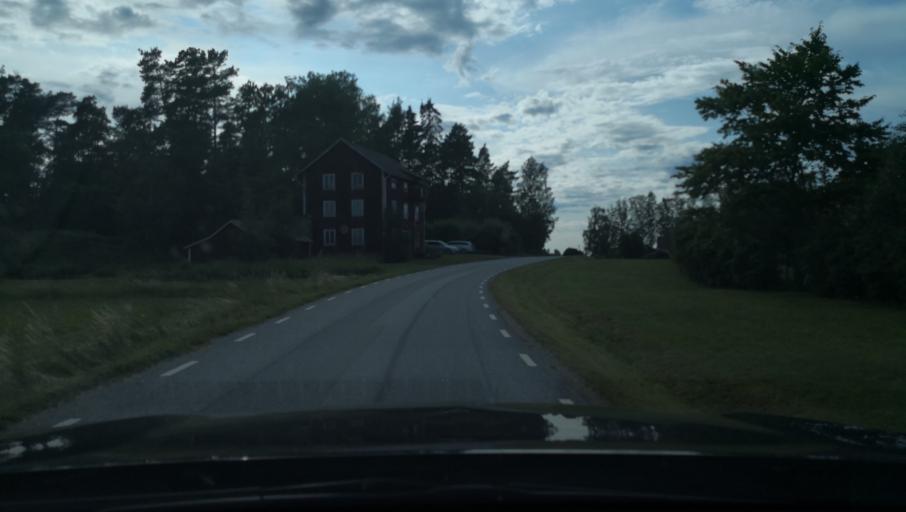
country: SE
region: Uppsala
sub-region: Enkopings Kommun
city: Orsundsbro
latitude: 59.6888
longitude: 17.3746
